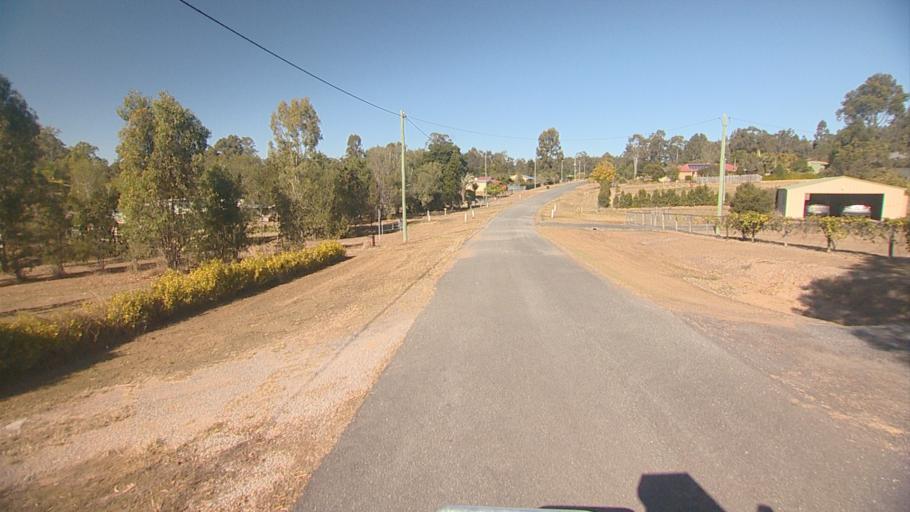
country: AU
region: Queensland
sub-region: Logan
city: Cedar Vale
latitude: -27.8673
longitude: 153.0073
